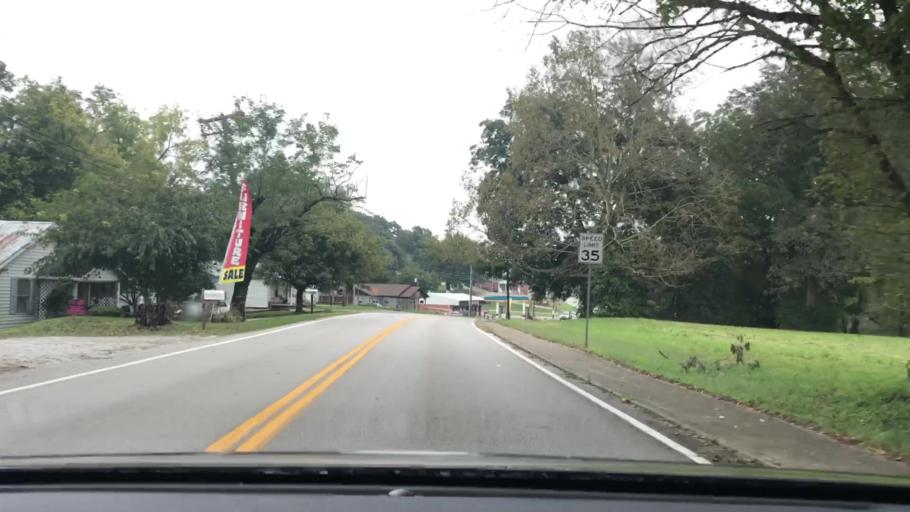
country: US
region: Kentucky
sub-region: Pulaski County
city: Somerset
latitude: 37.0899
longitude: -84.5910
